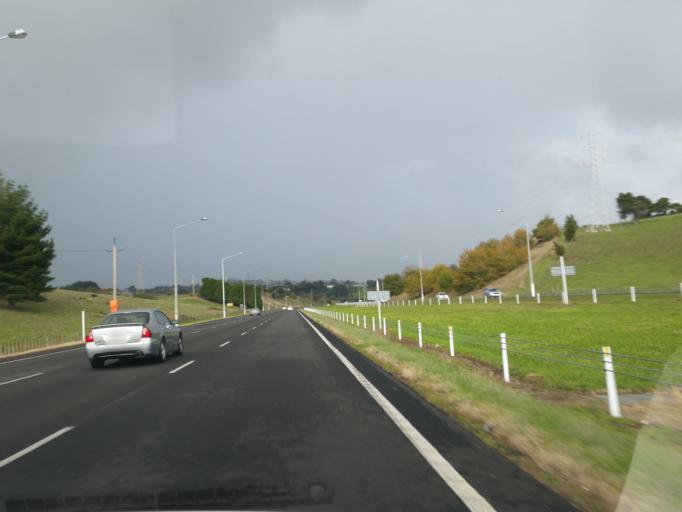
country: NZ
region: Auckland
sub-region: Auckland
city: Pukekohe East
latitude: -37.1616
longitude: 174.9812
